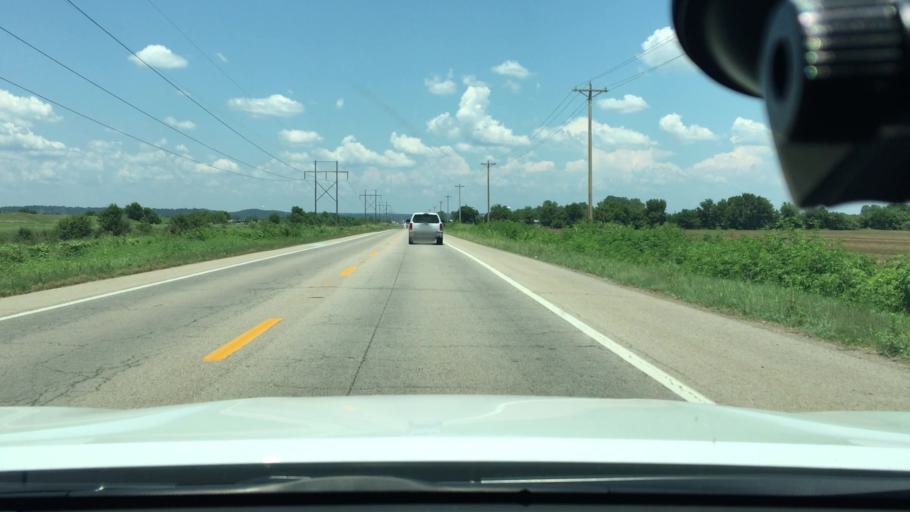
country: US
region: Arkansas
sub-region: Crawford County
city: Van Buren
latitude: 35.3966
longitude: -94.3303
